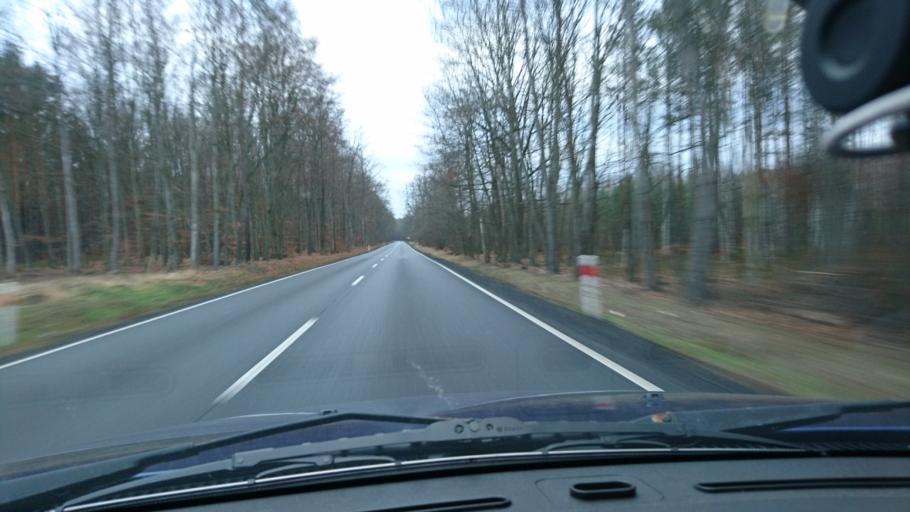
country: PL
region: Opole Voivodeship
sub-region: Powiat oleski
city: Olesno
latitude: 50.9320
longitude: 18.3330
